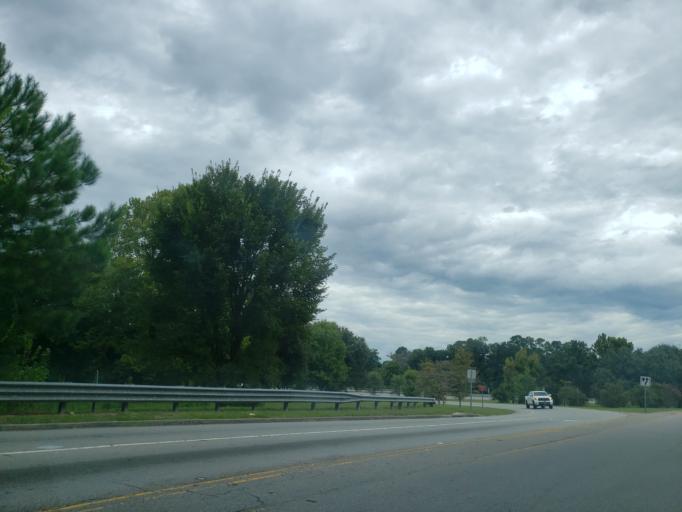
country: US
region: Georgia
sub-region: Chatham County
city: Thunderbolt
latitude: 32.0343
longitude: -81.0815
